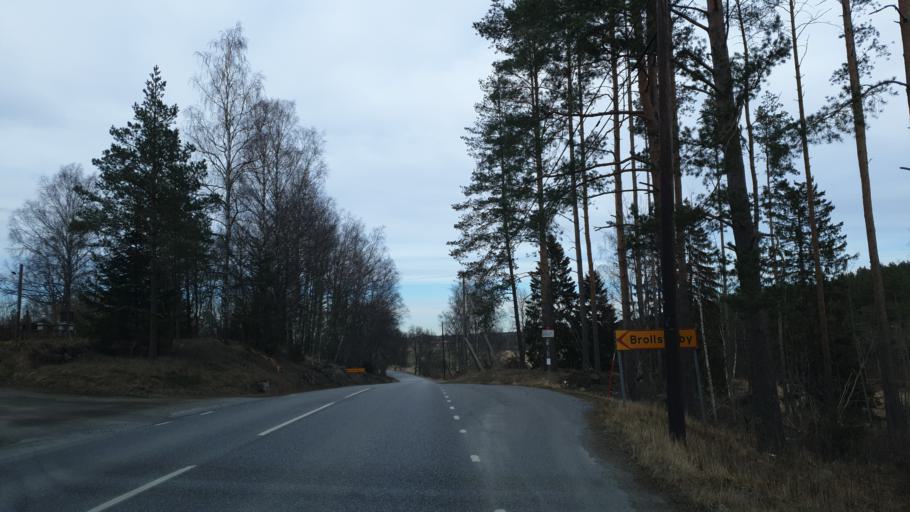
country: SE
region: Stockholm
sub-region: Osterakers Kommun
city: Akersberga
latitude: 59.5929
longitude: 18.3022
